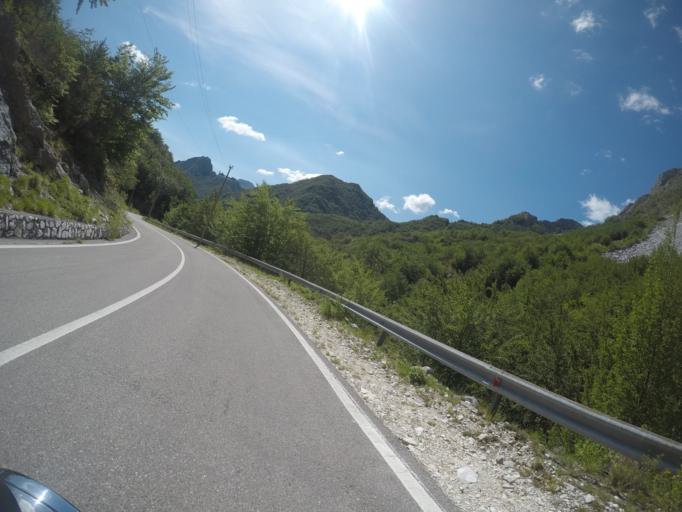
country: IT
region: Tuscany
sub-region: Provincia di Lucca
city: Seravezza
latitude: 44.0597
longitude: 10.2393
